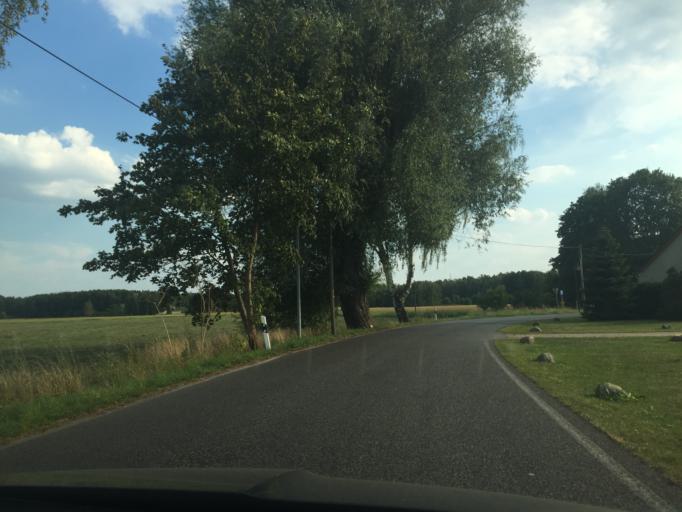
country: DE
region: Brandenburg
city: Spreenhagen
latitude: 52.3519
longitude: 13.8392
